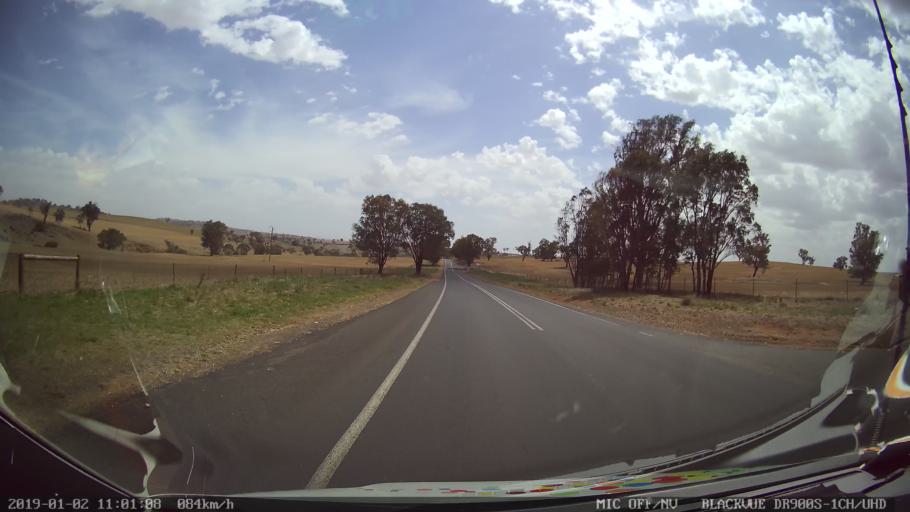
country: AU
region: New South Wales
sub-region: Young
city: Young
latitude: -34.6010
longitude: 148.3173
